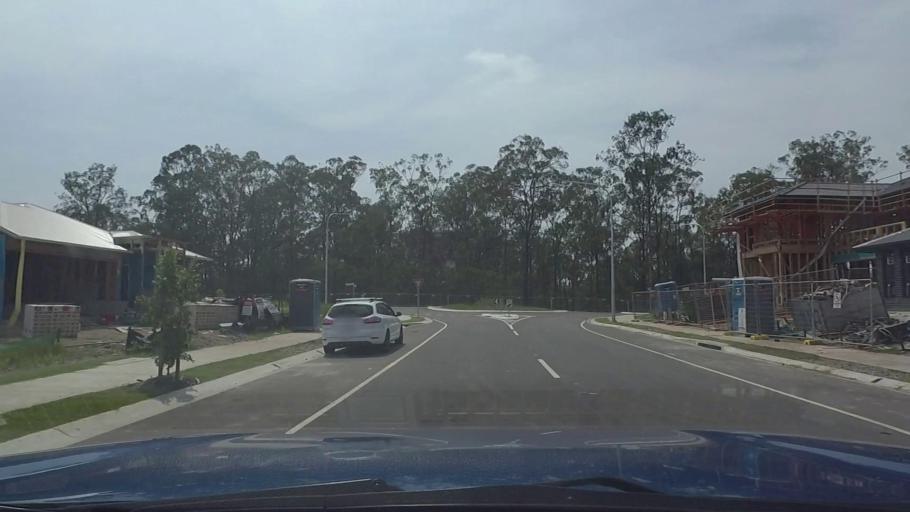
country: AU
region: Queensland
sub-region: Logan
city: Logan Reserve
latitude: -27.7049
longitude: 153.1060
